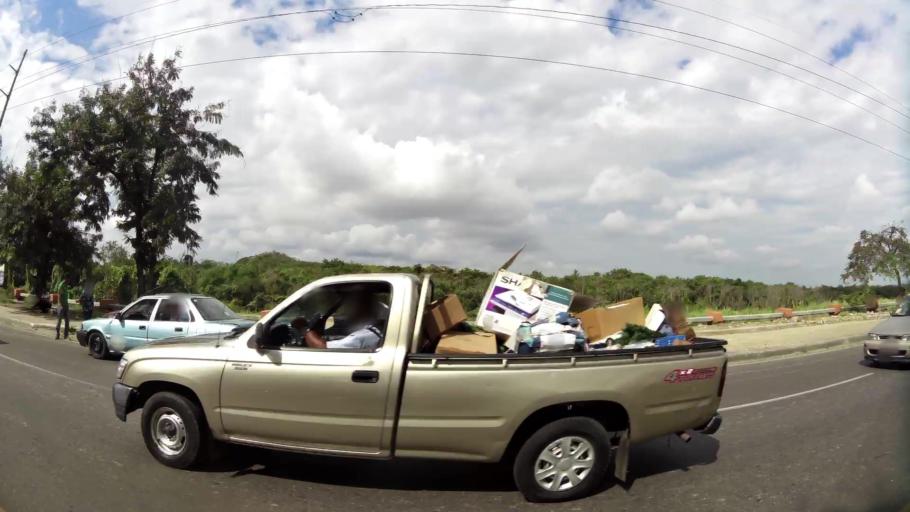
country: DO
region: Santiago
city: Santiago de los Caballeros
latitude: 19.4661
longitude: -70.7134
